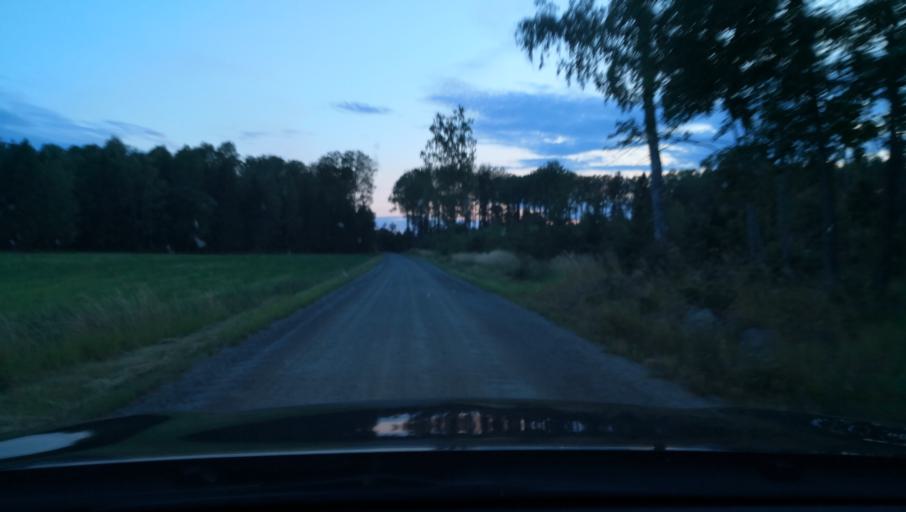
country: SE
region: Uppsala
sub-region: Osthammars Kommun
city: Bjorklinge
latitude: 60.0034
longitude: 17.3483
